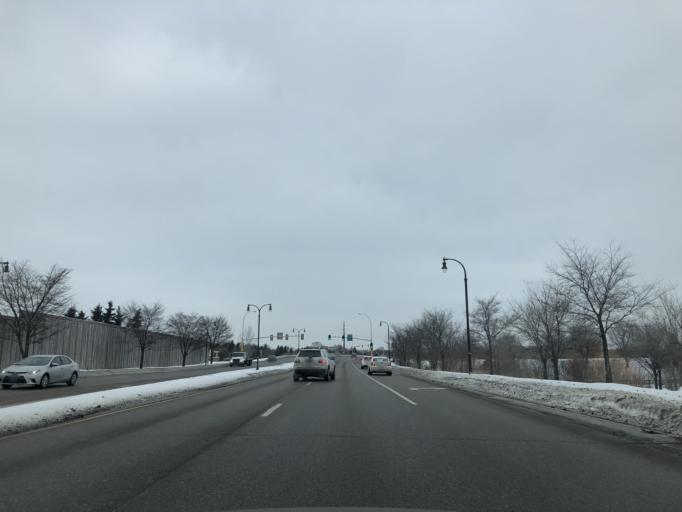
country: US
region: Minnesota
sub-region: Hennepin County
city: Robbinsdale
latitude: 45.0345
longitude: -93.3409
